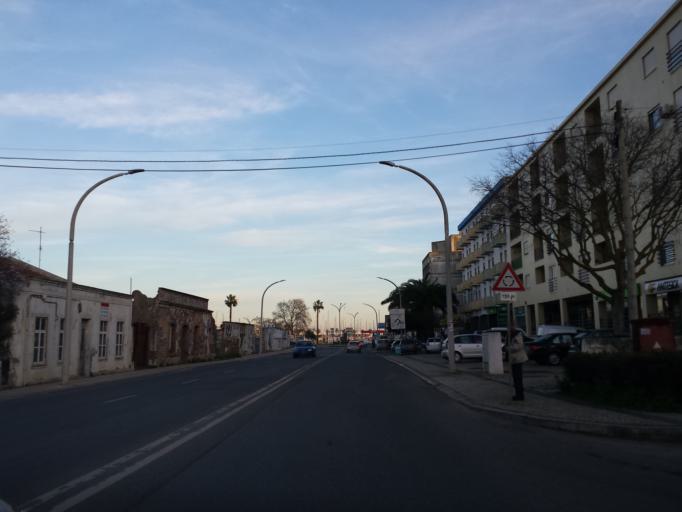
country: PT
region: Faro
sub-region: Lagos
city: Lagos
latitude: 37.1109
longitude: -8.6793
